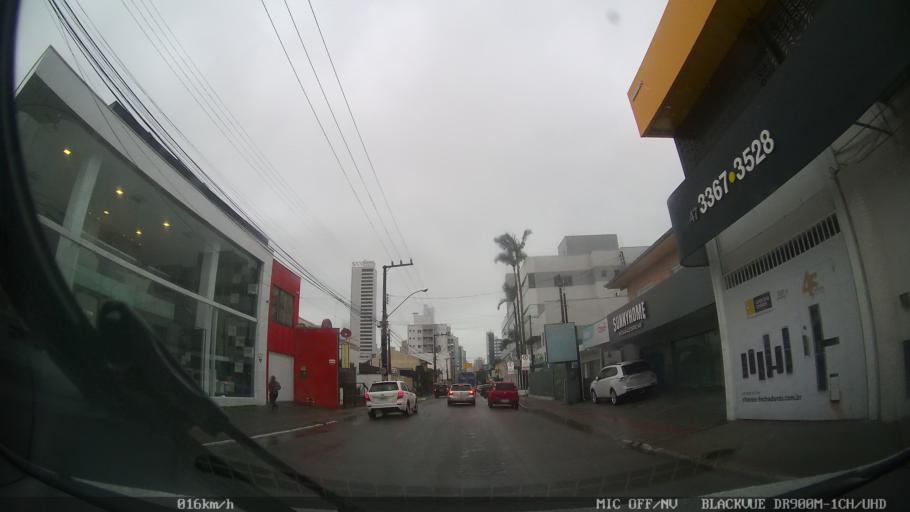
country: BR
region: Santa Catarina
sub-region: Balneario Camboriu
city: Balneario Camboriu
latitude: -26.9941
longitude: -48.6410
